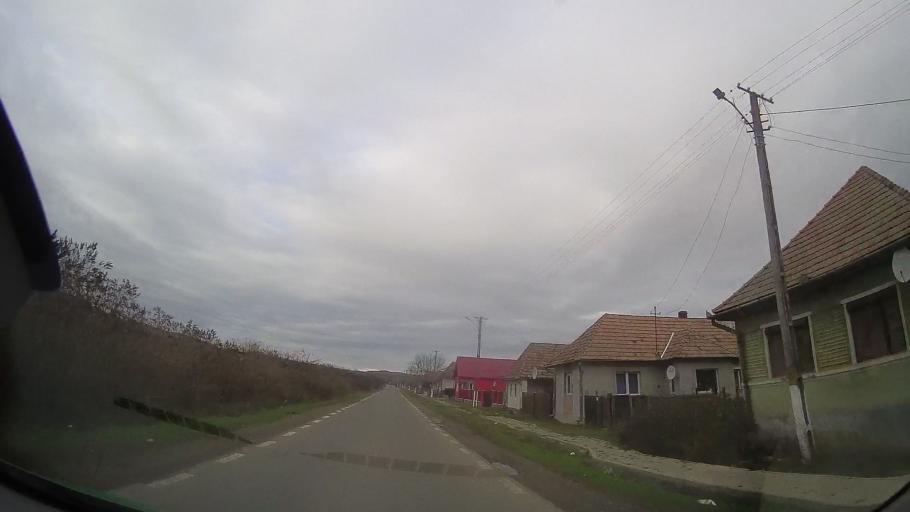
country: RO
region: Mures
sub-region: Comuna Faragau
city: Faragau
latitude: 46.7759
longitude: 24.5582
